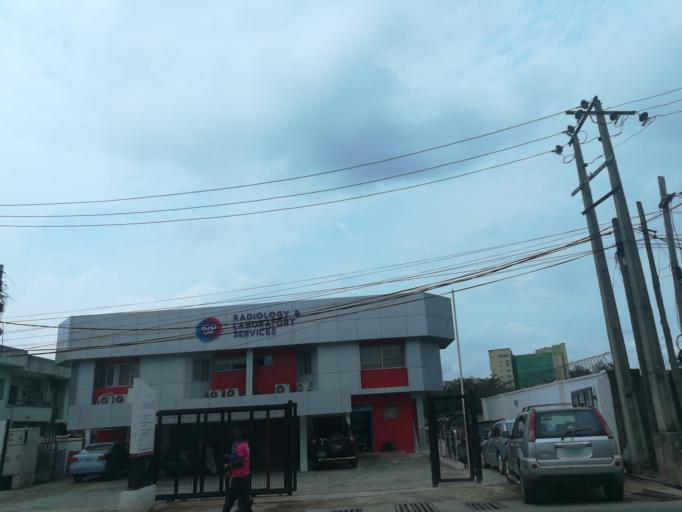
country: NG
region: Lagos
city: Ojota
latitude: 6.5854
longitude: 3.3646
